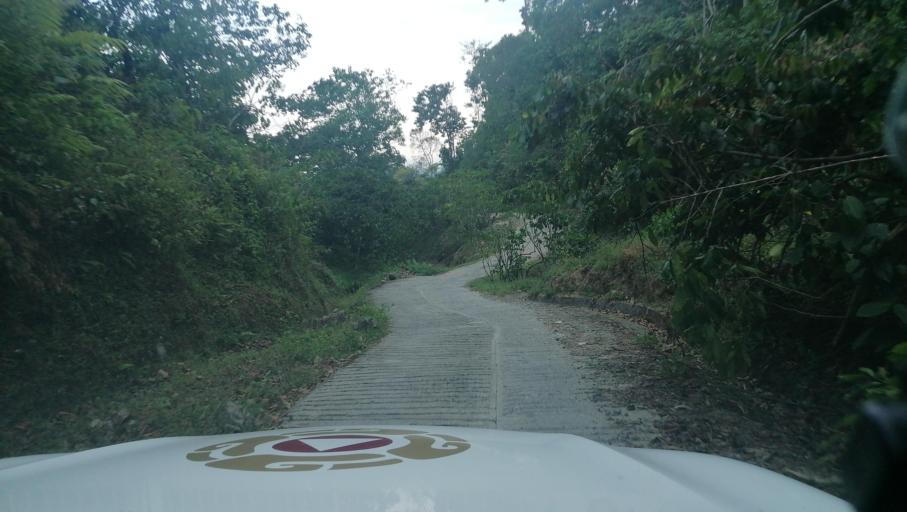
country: MX
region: Chiapas
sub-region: Cacahoatan
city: Benito Juarez
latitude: 15.0972
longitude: -92.2202
